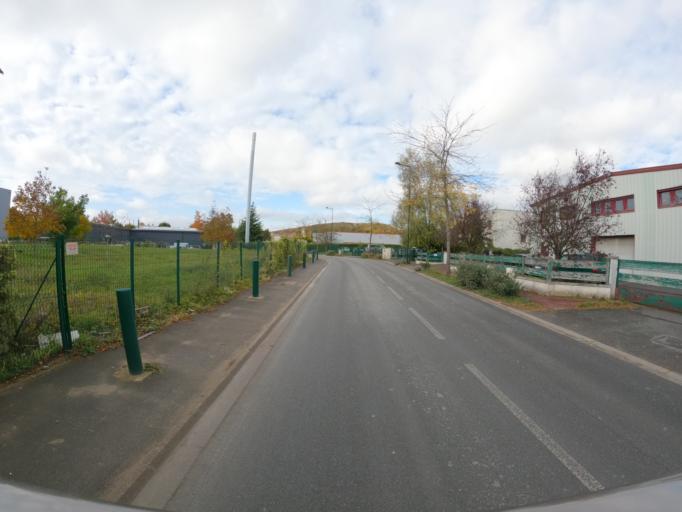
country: FR
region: Ile-de-France
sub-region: Departement de Seine-et-Marne
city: Chelles
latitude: 48.8925
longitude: 2.5942
